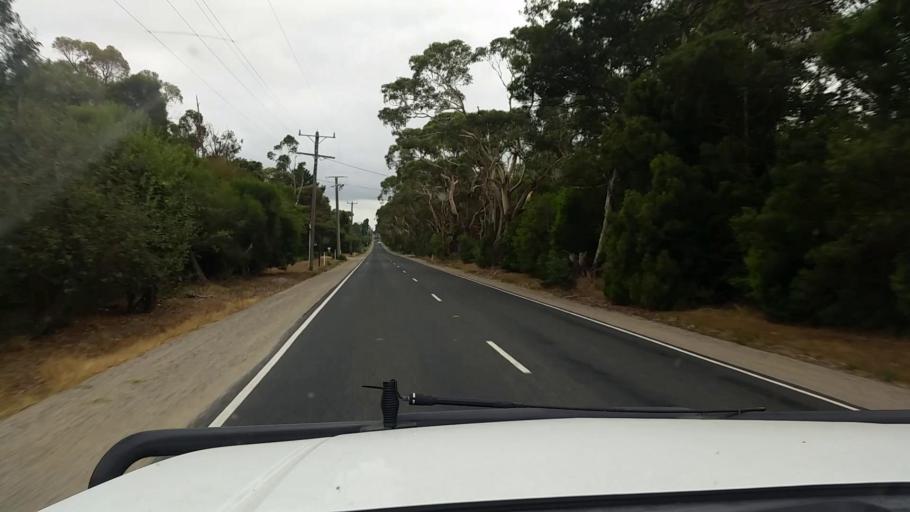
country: AU
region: Victoria
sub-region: Mornington Peninsula
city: Tyabb
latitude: -38.2714
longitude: 145.1456
